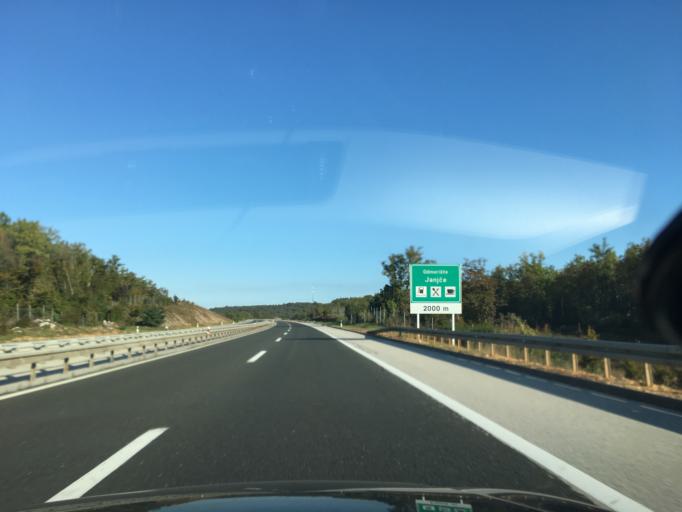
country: HR
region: Licko-Senjska
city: Gospic
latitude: 44.7306
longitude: 15.3836
